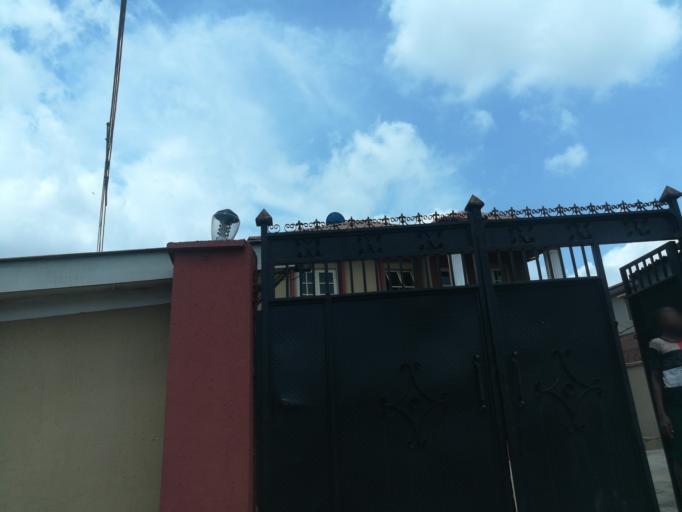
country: NG
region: Lagos
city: Somolu
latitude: 6.5380
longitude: 3.3647
